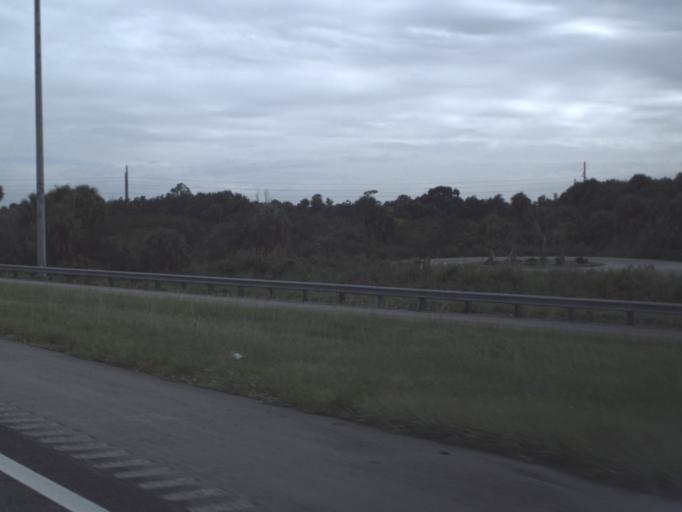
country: US
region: Florida
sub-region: Lee County
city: Tice
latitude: 26.7127
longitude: -81.8100
